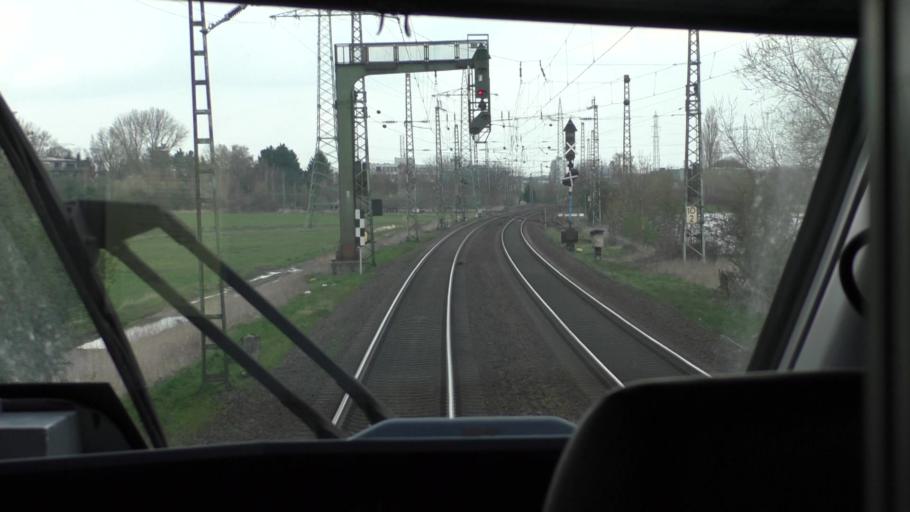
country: DE
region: North Rhine-Westphalia
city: Bruhl
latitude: 50.8666
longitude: 6.9086
